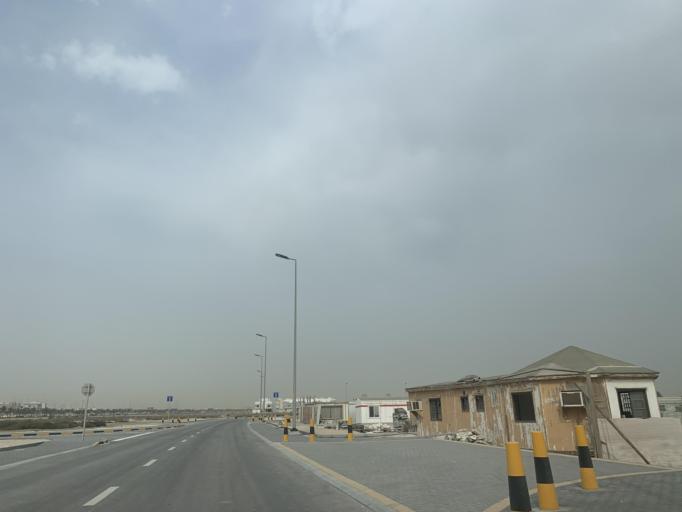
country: BH
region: Northern
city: Madinat `Isa
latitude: 26.1863
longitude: 50.5089
